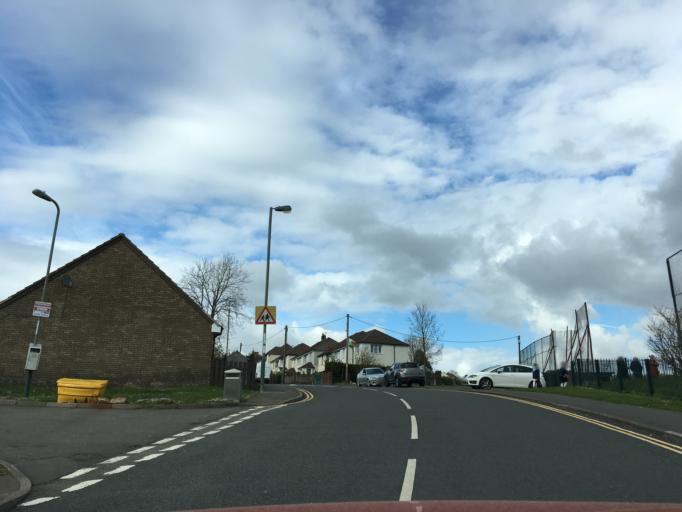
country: GB
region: Wales
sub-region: Caerphilly County Borough
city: Rhymney
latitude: 51.7417
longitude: -3.2960
